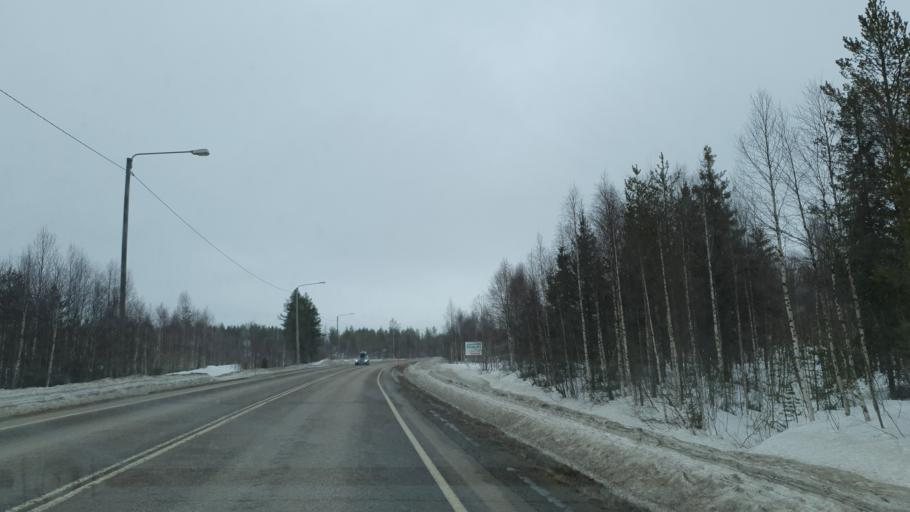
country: FI
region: Lapland
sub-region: Torniolaakso
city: Pello
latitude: 66.8864
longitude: 24.0754
